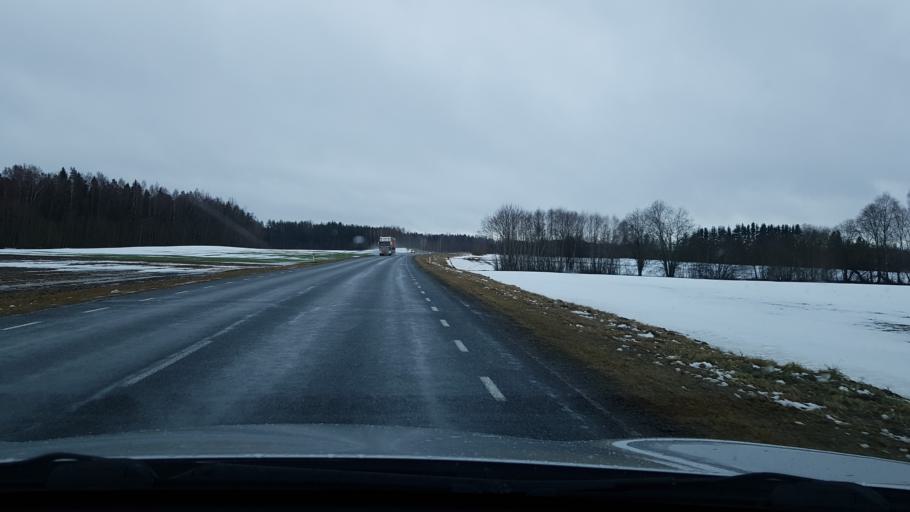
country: LV
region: Apes Novads
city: Ape
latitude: 57.6752
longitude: 26.7243
